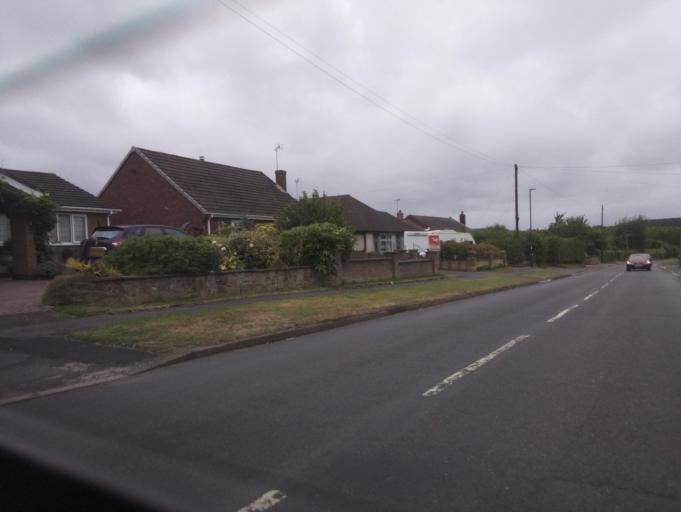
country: GB
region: England
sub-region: Derbyshire
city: Swadlincote
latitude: 52.7884
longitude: -1.5279
